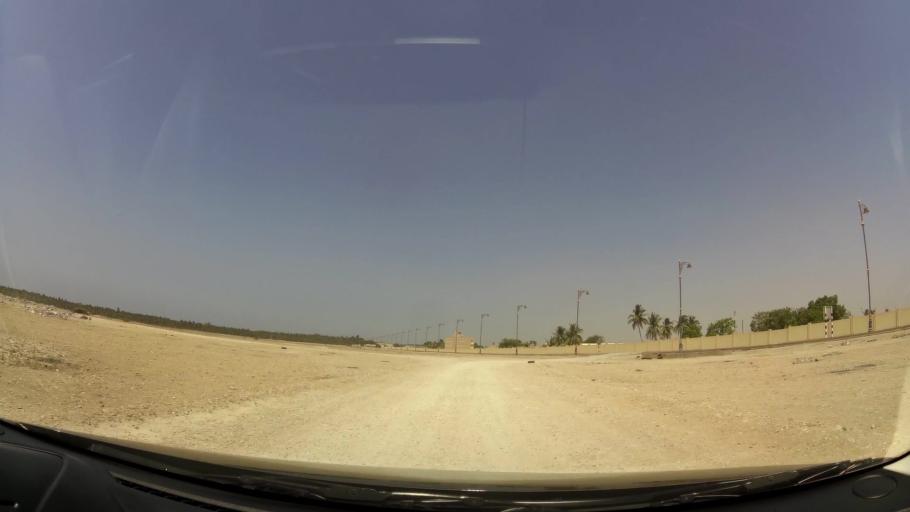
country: OM
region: Zufar
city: Salalah
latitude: 17.0481
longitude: 54.2235
